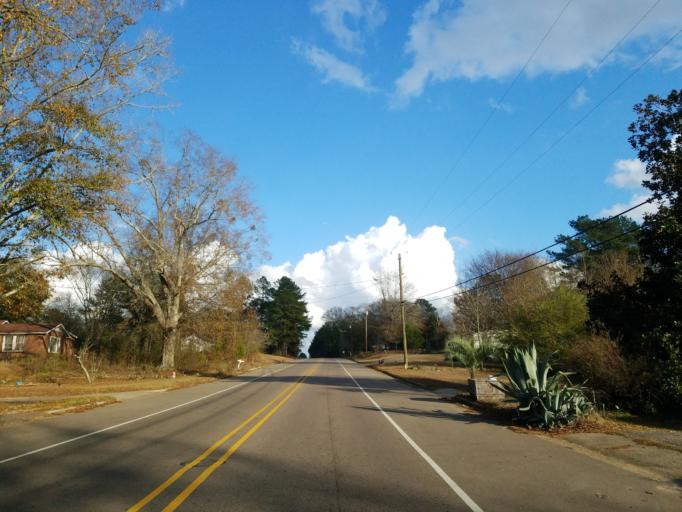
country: US
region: Mississippi
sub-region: Jones County
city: Sharon
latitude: 31.7880
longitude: -89.0440
